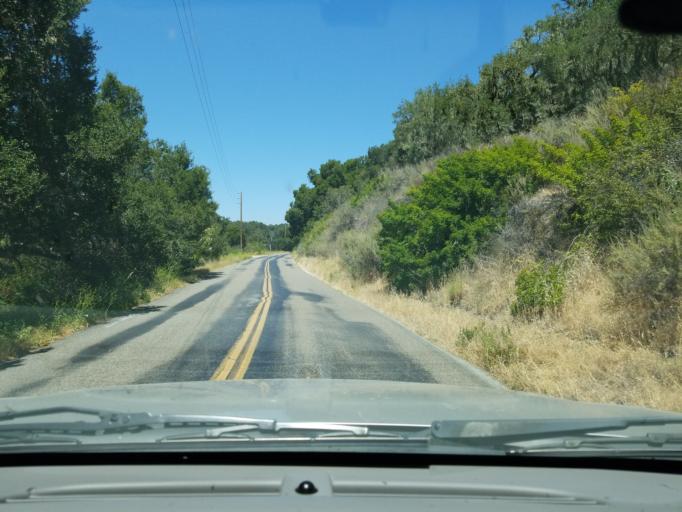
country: US
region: California
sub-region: Monterey County
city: Carmel Valley Village
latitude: 36.4246
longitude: -121.6182
